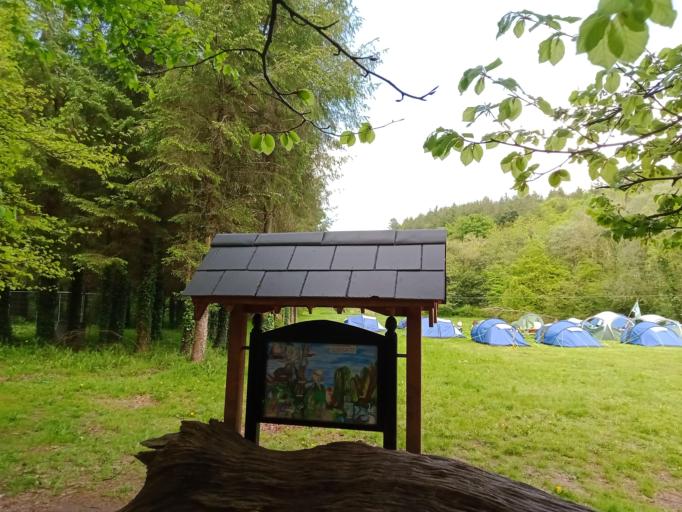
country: IE
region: Leinster
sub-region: Kilkenny
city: Castlecomer
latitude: 52.8100
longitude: -7.2043
